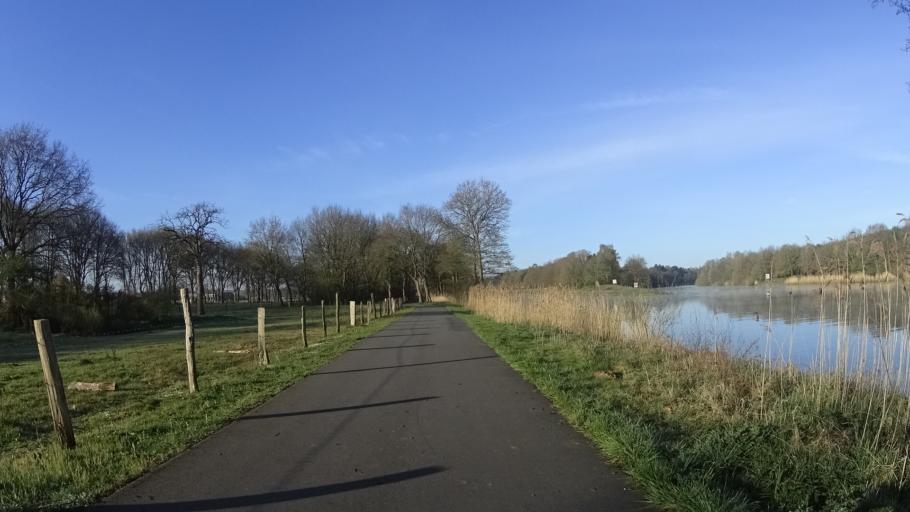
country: DE
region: Lower Saxony
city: Niederlangen
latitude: 52.8385
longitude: 7.2846
